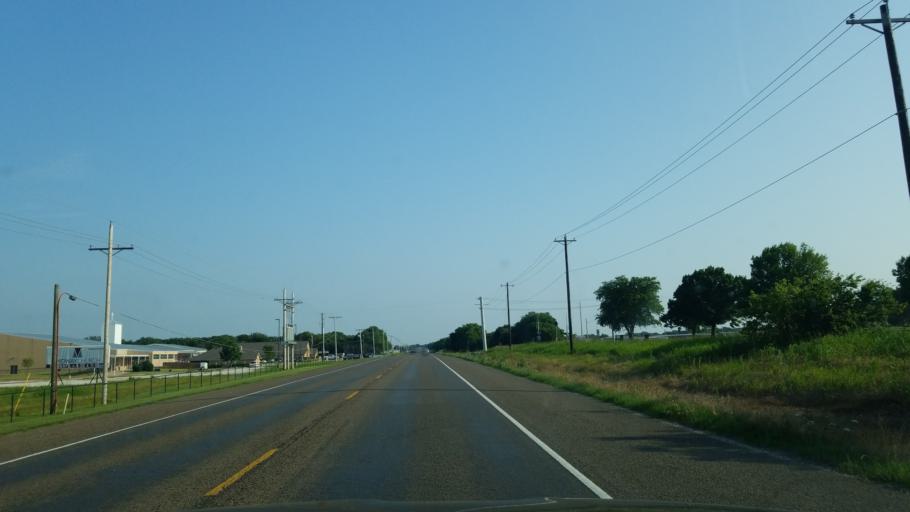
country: US
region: Texas
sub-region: Denton County
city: Aubrey
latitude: 33.3430
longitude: -96.9689
